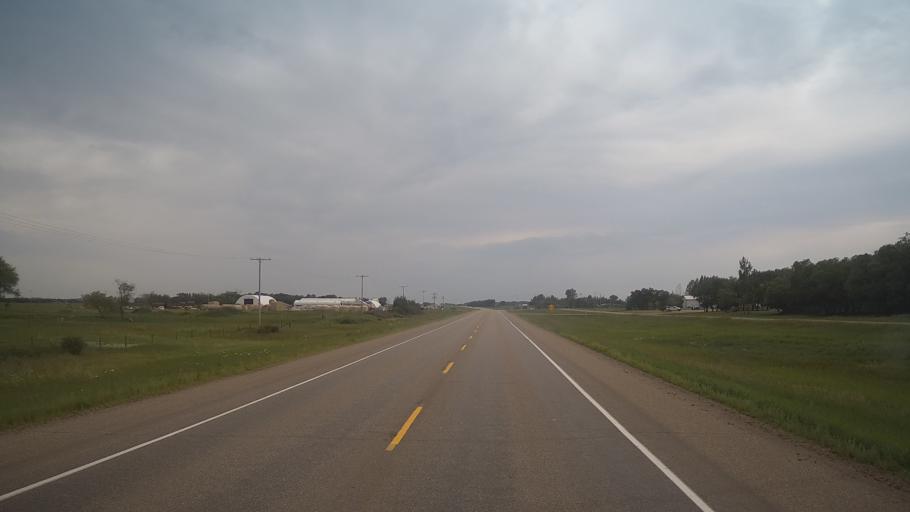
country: CA
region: Saskatchewan
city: Langham
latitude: 52.1289
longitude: -107.2218
